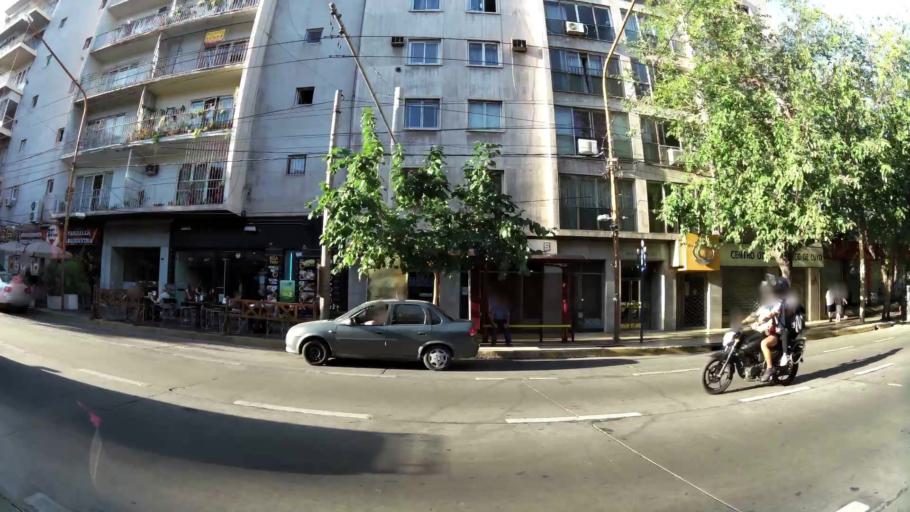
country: AR
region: Mendoza
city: Mendoza
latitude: -32.8951
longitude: -68.8400
